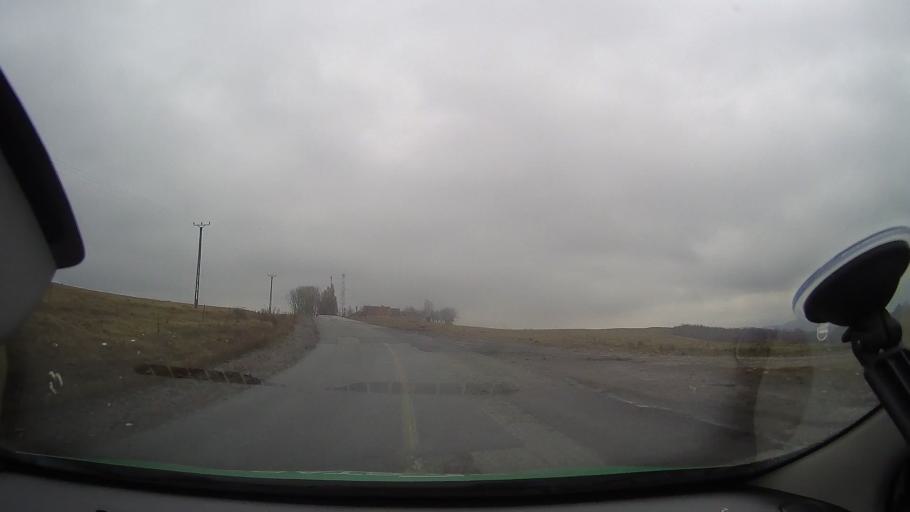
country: RO
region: Arad
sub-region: Comuna Halmagiu
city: Halmagiu
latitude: 46.2831
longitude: 22.5721
